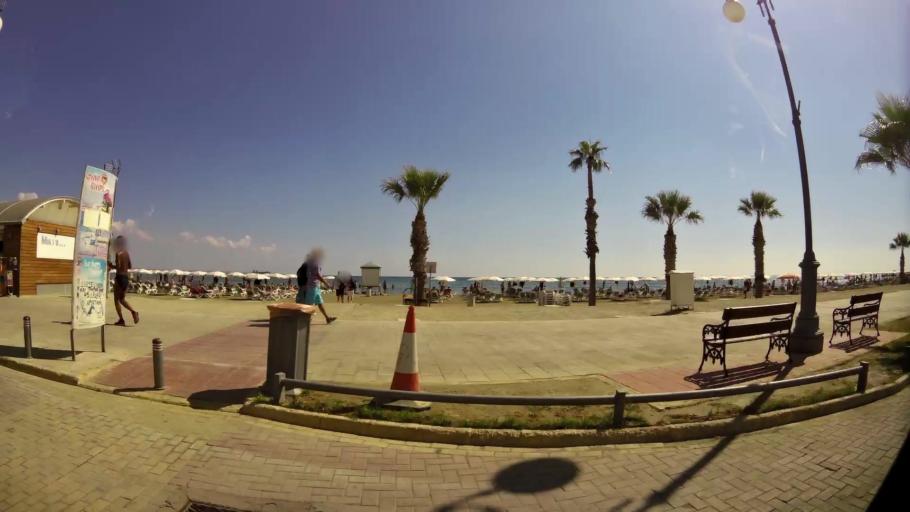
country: CY
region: Larnaka
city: Larnaca
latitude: 34.9125
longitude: 33.6382
